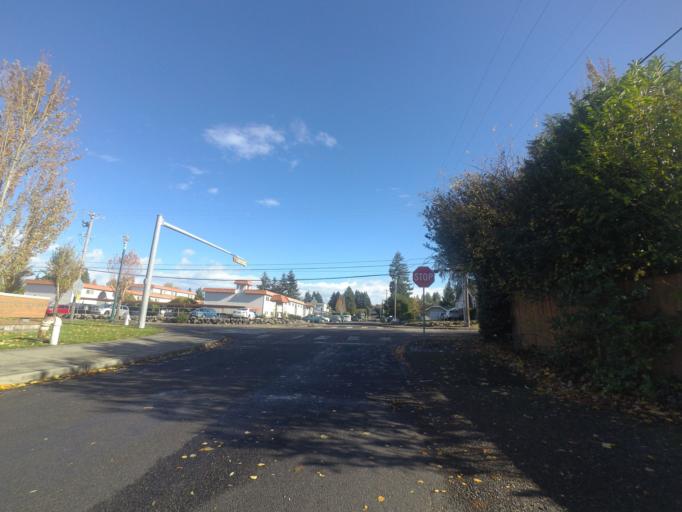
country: US
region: Washington
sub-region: Pierce County
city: University Place
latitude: 47.2335
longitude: -122.5507
